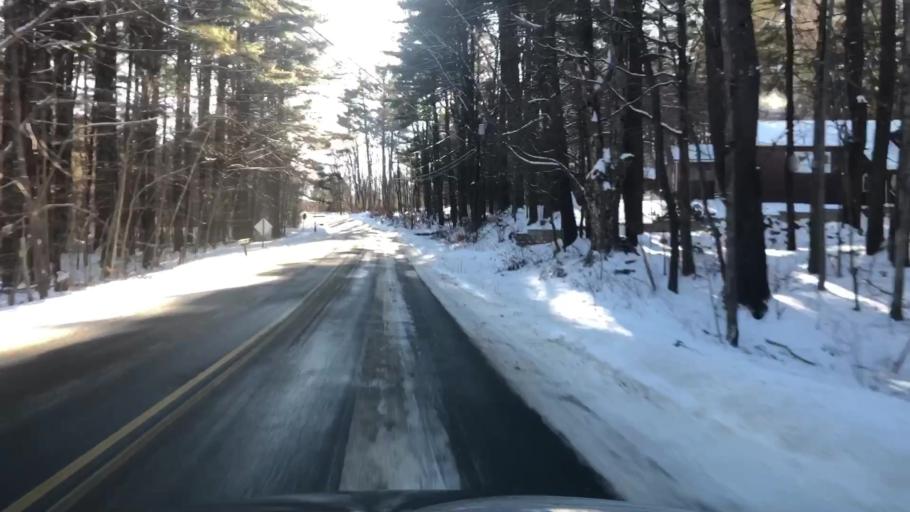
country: US
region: New Hampshire
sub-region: Hillsborough County
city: Wilton
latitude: 42.8193
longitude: -71.7206
